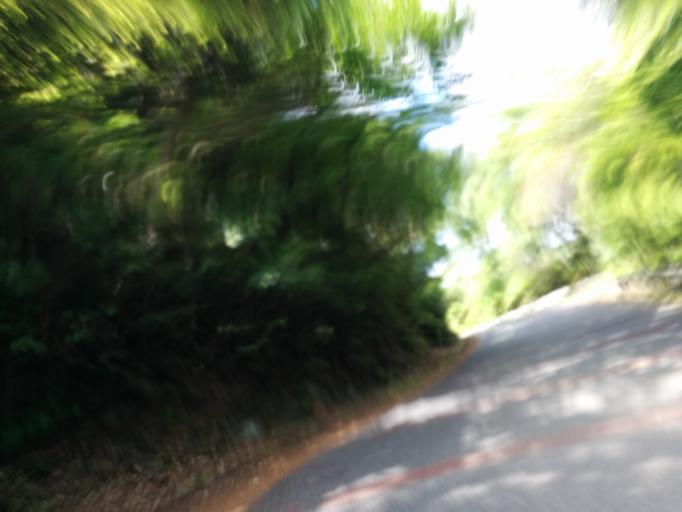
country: JP
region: Gifu
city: Inuyama
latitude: 35.3446
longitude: 136.9878
